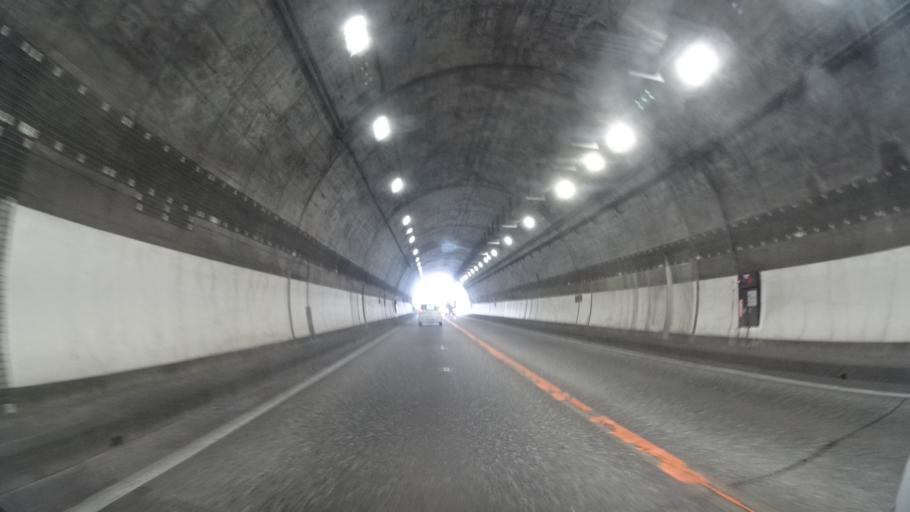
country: JP
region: Tottori
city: Tottori
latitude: 35.5214
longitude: 134.1006
